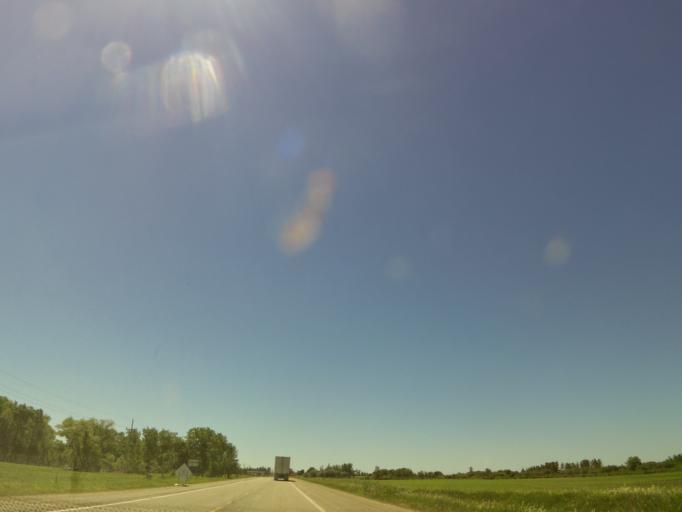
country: US
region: Minnesota
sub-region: Mahnomen County
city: Mahnomen
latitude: 47.1183
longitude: -95.9270
